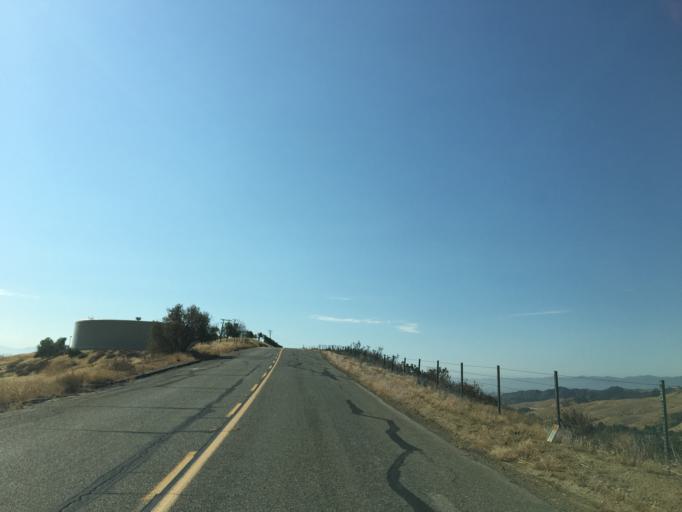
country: US
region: California
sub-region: Los Angeles County
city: Castaic
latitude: 34.5204
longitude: -118.6384
